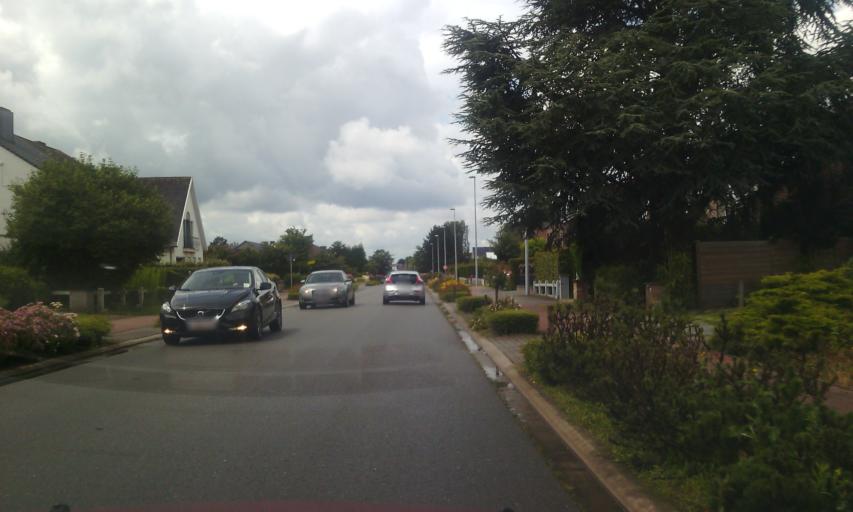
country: BE
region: Flanders
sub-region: Provincie Oost-Vlaanderen
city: Wetteren
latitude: 51.0127
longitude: 3.8795
